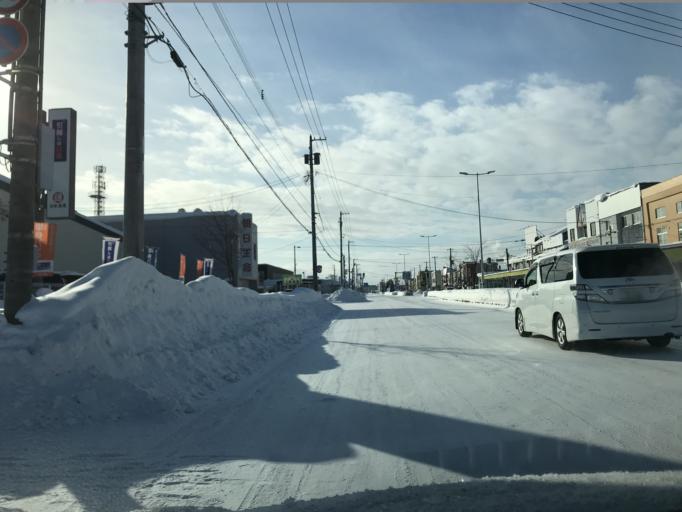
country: JP
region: Hokkaido
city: Nayoro
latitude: 44.3504
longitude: 142.4639
